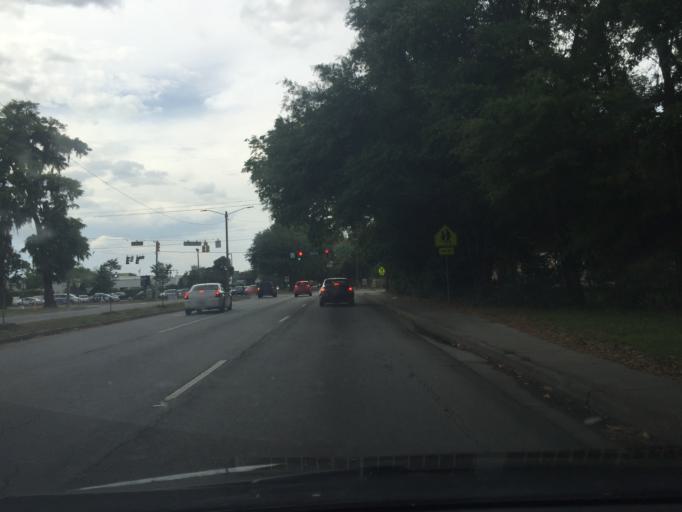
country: US
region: Georgia
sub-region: Chatham County
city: Montgomery
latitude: 31.9875
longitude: -81.1288
